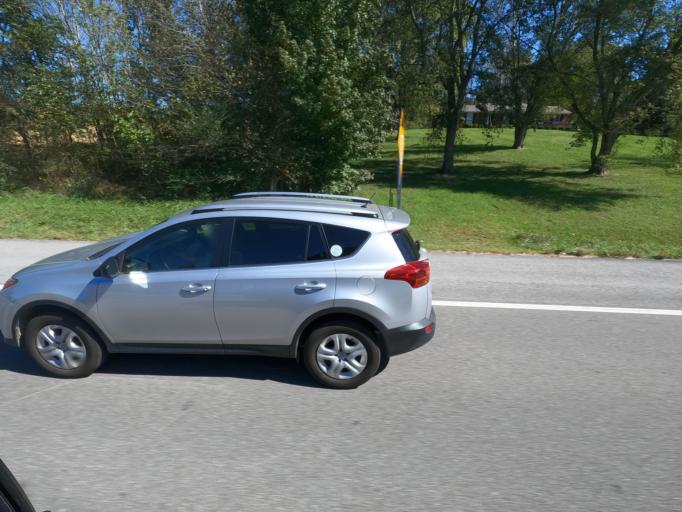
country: US
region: Tennessee
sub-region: Maury County
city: Mount Pleasant
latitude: 35.4181
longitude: -87.2820
